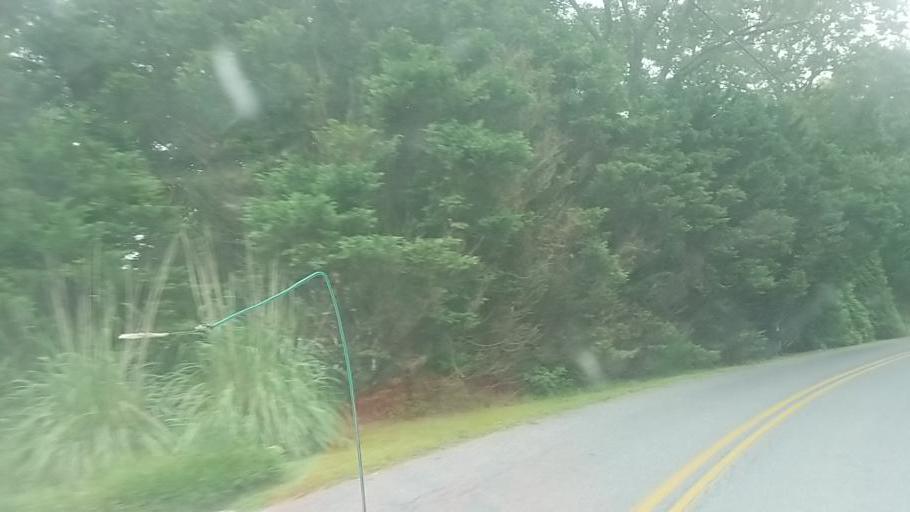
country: US
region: Delaware
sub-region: Sussex County
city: Selbyville
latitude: 38.4254
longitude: -75.1917
